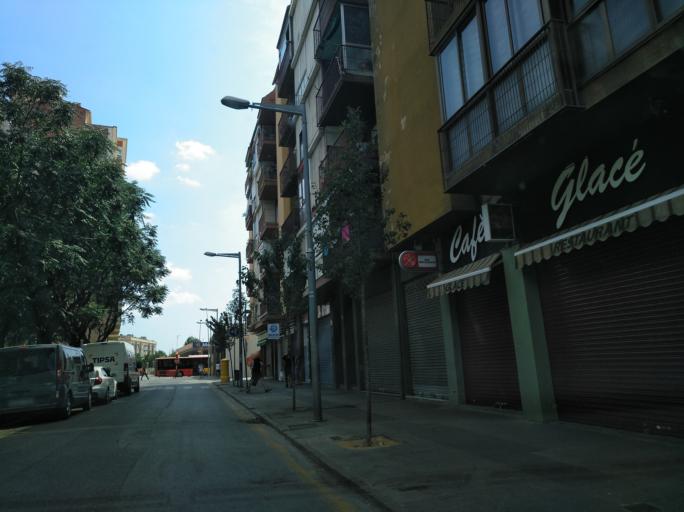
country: ES
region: Catalonia
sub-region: Provincia de Girona
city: Salt
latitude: 41.9747
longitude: 2.7984
